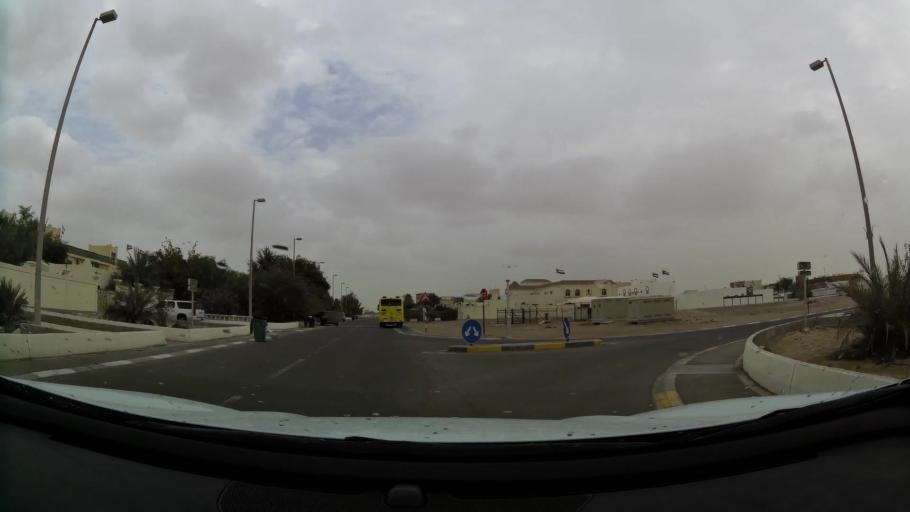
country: AE
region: Abu Dhabi
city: Abu Dhabi
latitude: 24.3336
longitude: 54.6370
